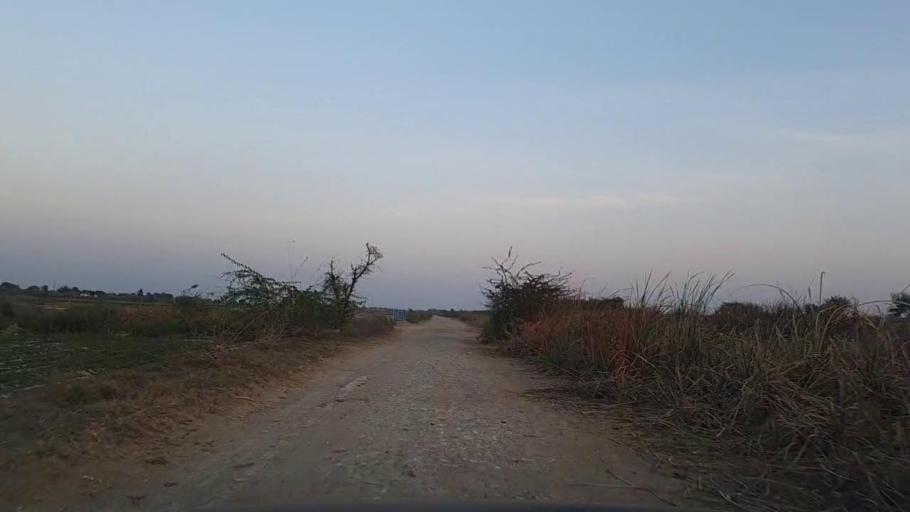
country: PK
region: Sindh
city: Tando Mittha Khan
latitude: 25.9419
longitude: 69.1379
